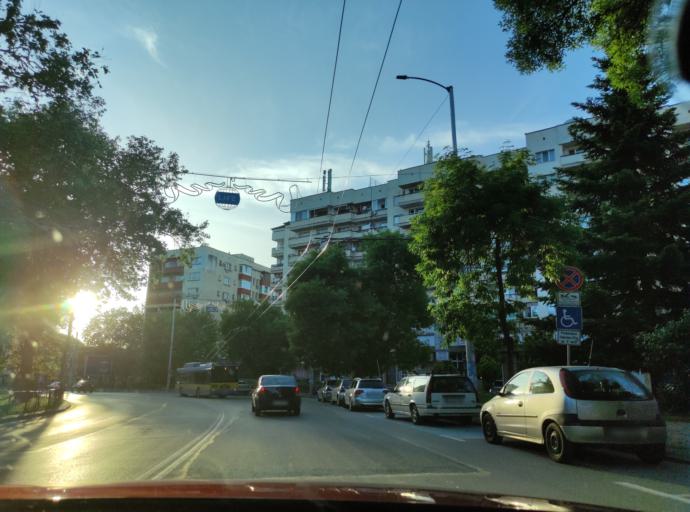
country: BG
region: Pleven
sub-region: Obshtina Pleven
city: Pleven
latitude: 43.4129
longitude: 24.6184
